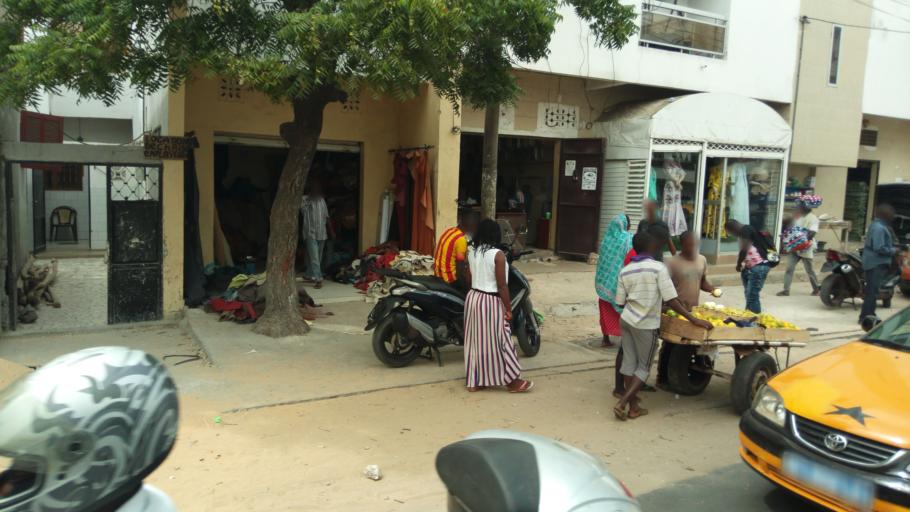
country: SN
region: Dakar
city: Dakar
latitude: 14.6857
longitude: -17.4499
